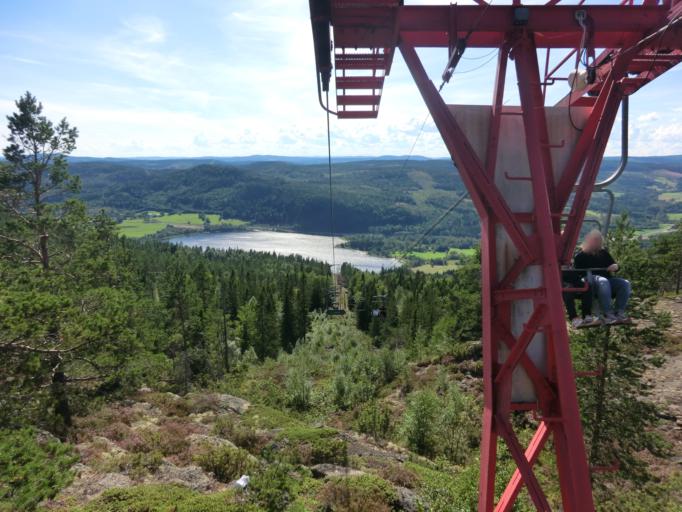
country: SE
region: Vaesternorrland
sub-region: Kramfors Kommun
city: Nordingra
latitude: 63.0755
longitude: 18.3479
